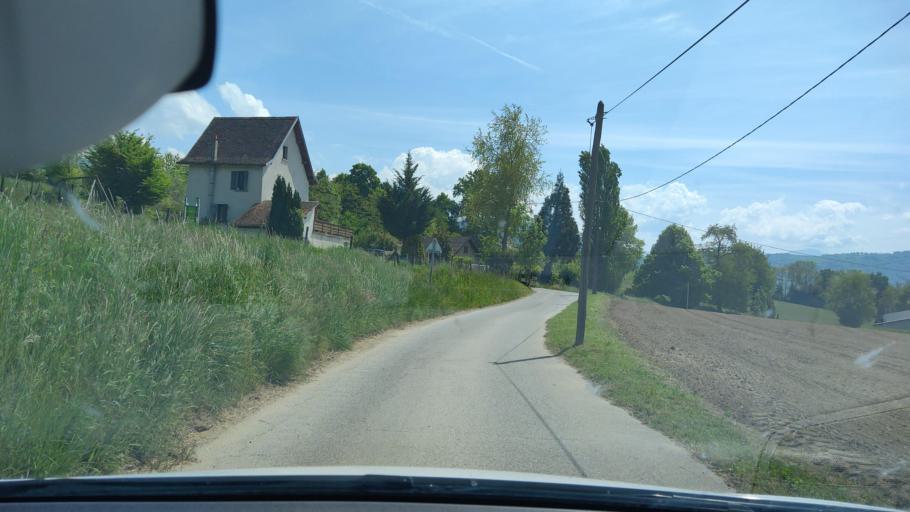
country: FR
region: Rhone-Alpes
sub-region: Departement de la Savoie
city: Domessin
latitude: 45.5230
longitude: 5.7160
